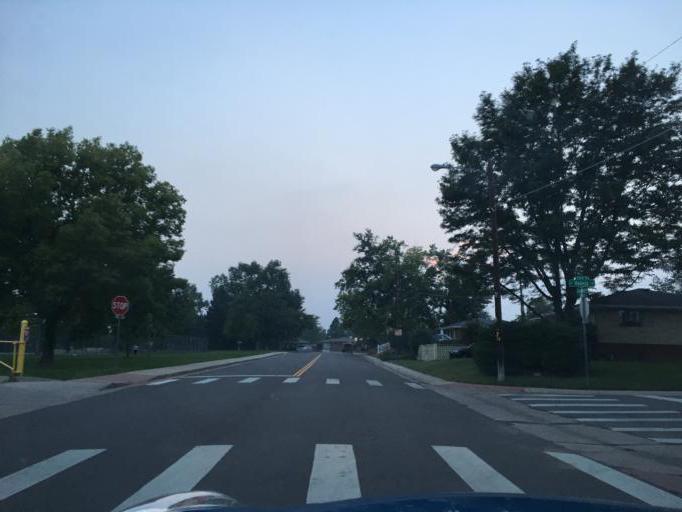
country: US
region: Colorado
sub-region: Arapahoe County
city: Sheridan
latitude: 39.6909
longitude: -105.0133
